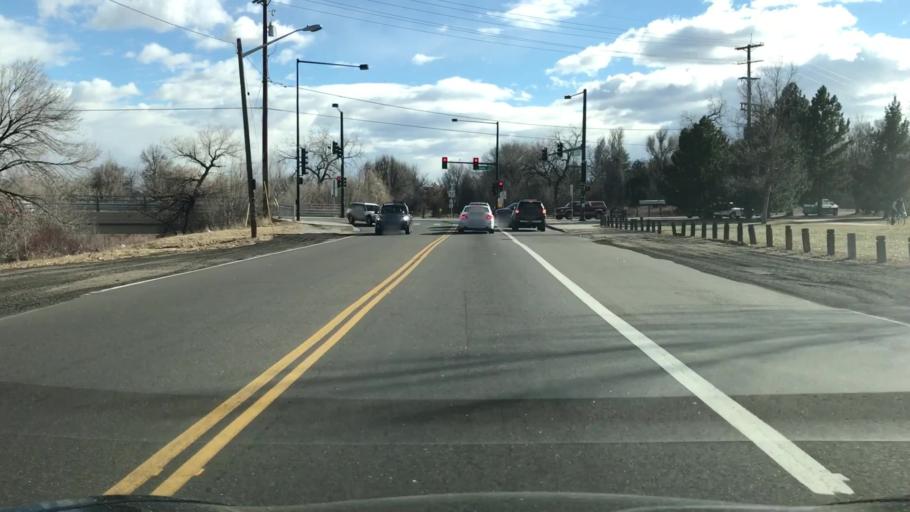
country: US
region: Colorado
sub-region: Arapahoe County
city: Glendale
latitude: 39.6963
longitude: -104.9230
